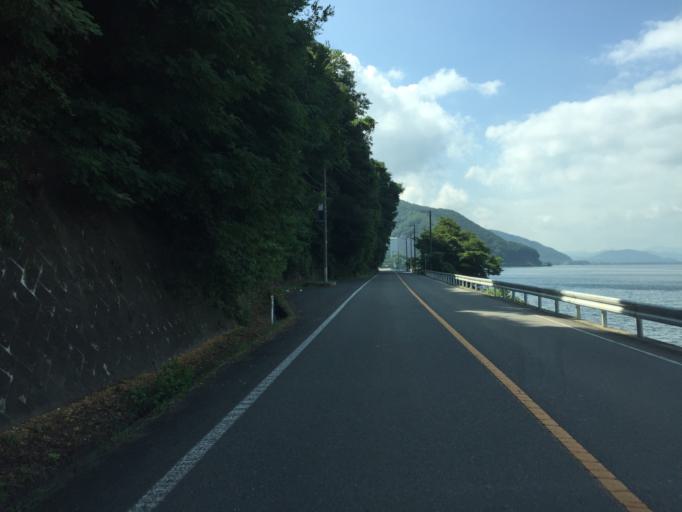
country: JP
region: Fukushima
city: Inawashiro
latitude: 37.4696
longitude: 140.1528
